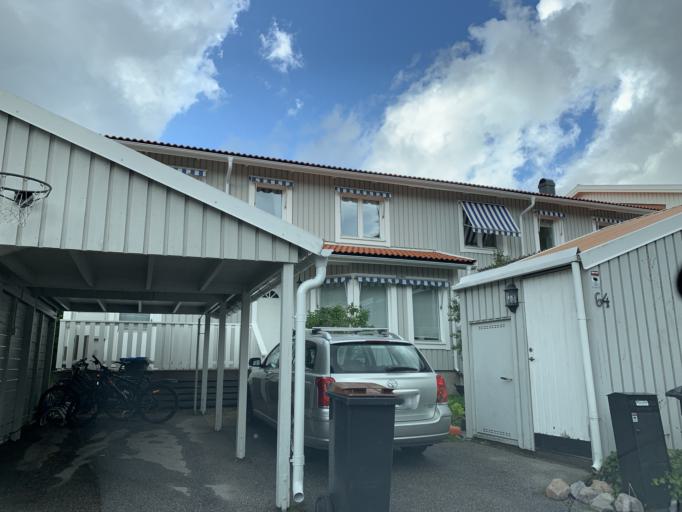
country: SE
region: Stockholm
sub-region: Taby Kommun
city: Taby
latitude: 59.4398
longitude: 18.0151
